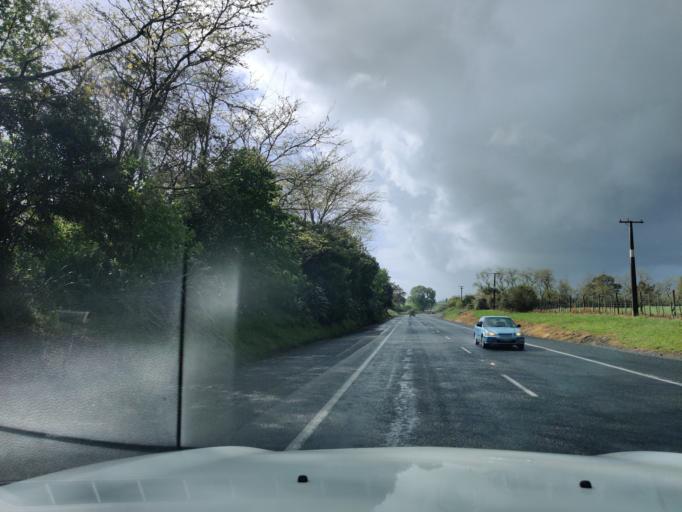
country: NZ
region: Waikato
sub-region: Waipa District
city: Cambridge
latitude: -37.9243
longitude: 175.5646
